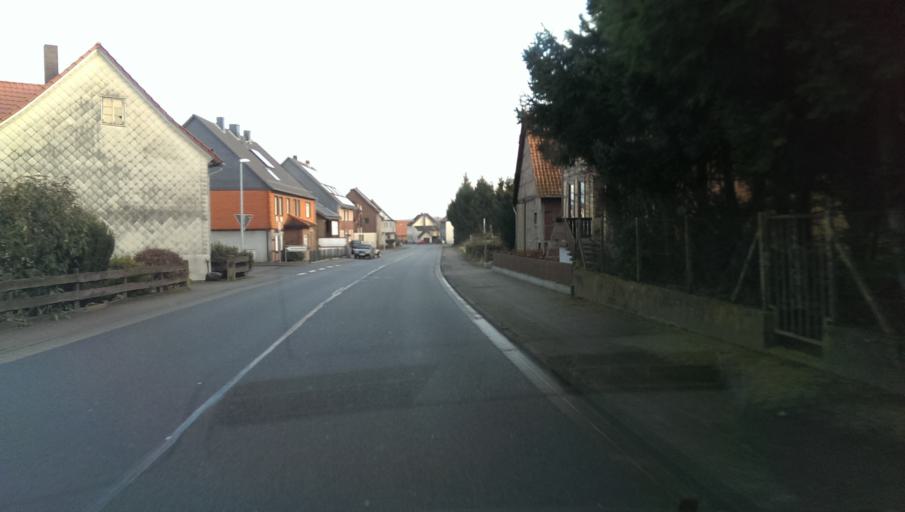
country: DE
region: Lower Saxony
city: Eimen
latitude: 51.8868
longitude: 9.7487
